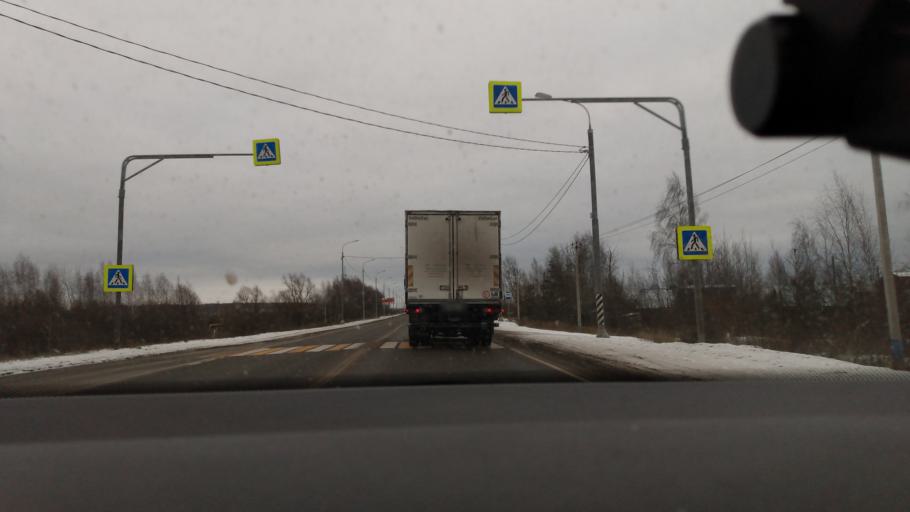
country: RU
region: Moskovskaya
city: Yegor'yevsk
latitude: 55.4092
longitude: 39.0517
